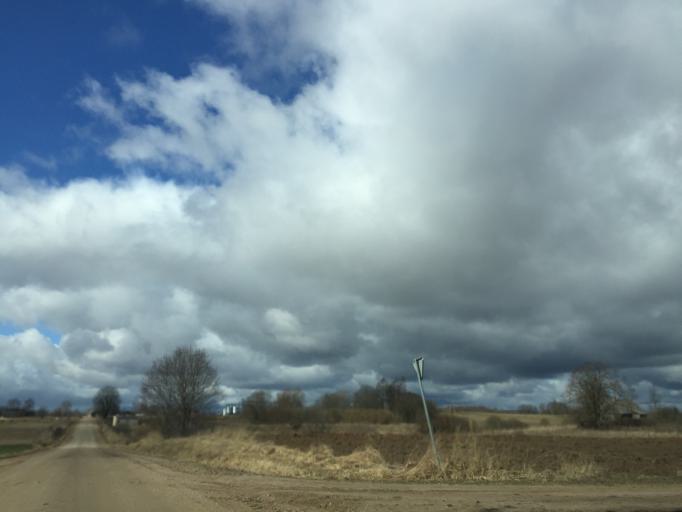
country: LV
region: Akniste
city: Akniste
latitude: 56.1004
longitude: 25.9719
